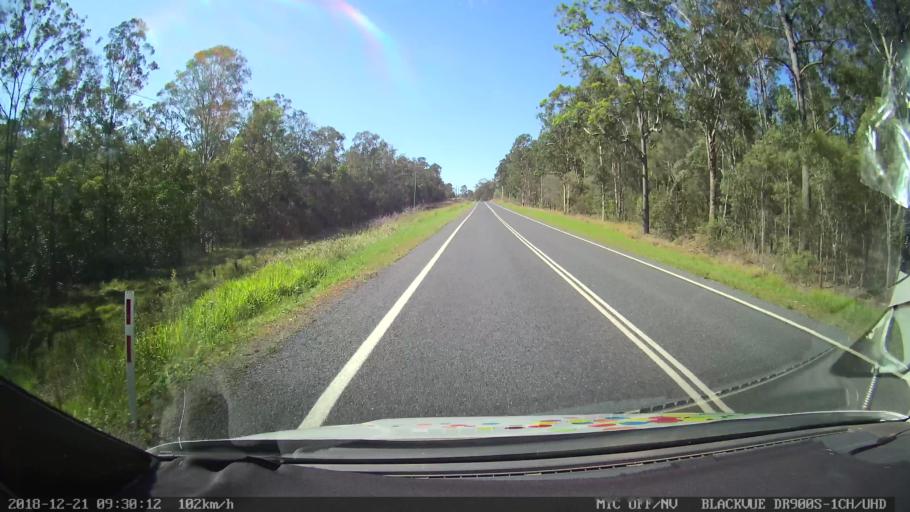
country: AU
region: New South Wales
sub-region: Clarence Valley
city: Maclean
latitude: -29.4431
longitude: 152.9917
